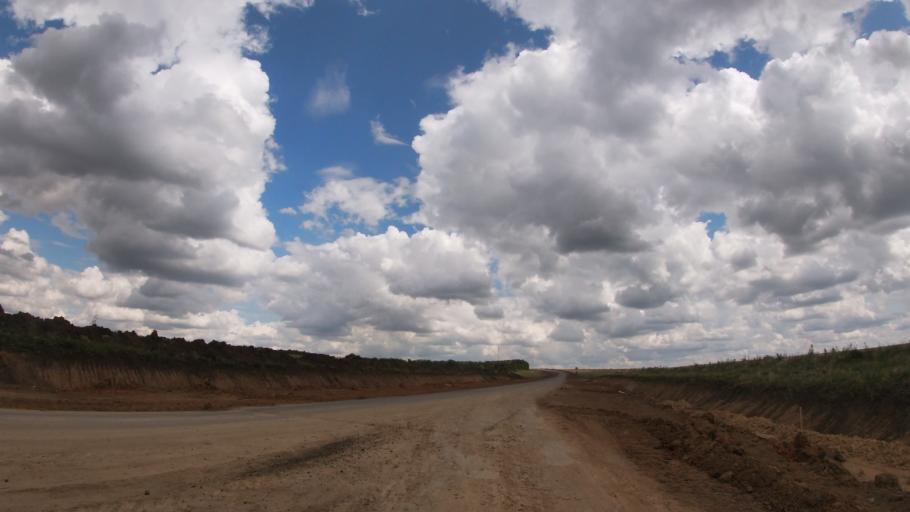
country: RU
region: Belgorod
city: Mayskiy
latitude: 50.5188
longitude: 36.4954
